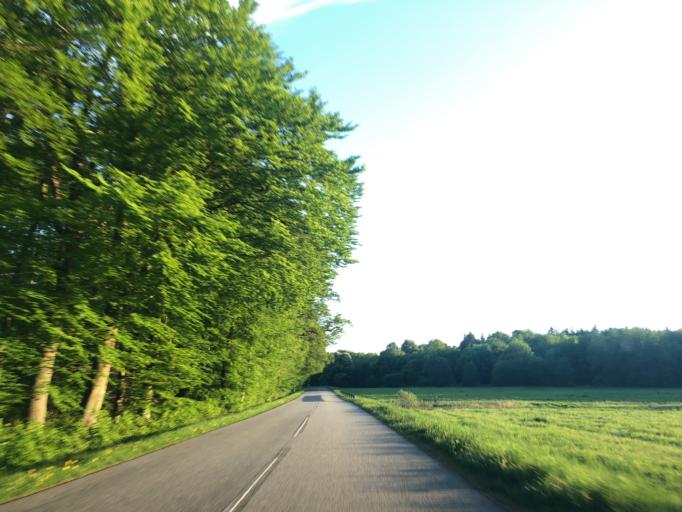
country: DK
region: Zealand
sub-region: Koge Kommune
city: Borup
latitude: 55.4332
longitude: 11.9388
